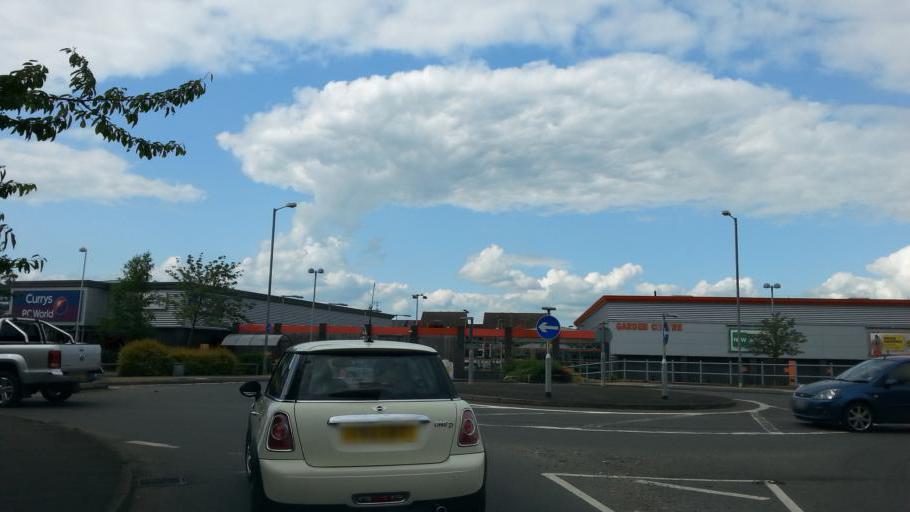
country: GB
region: England
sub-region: Worcestershire
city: Evesham
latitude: 52.0777
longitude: -1.9391
